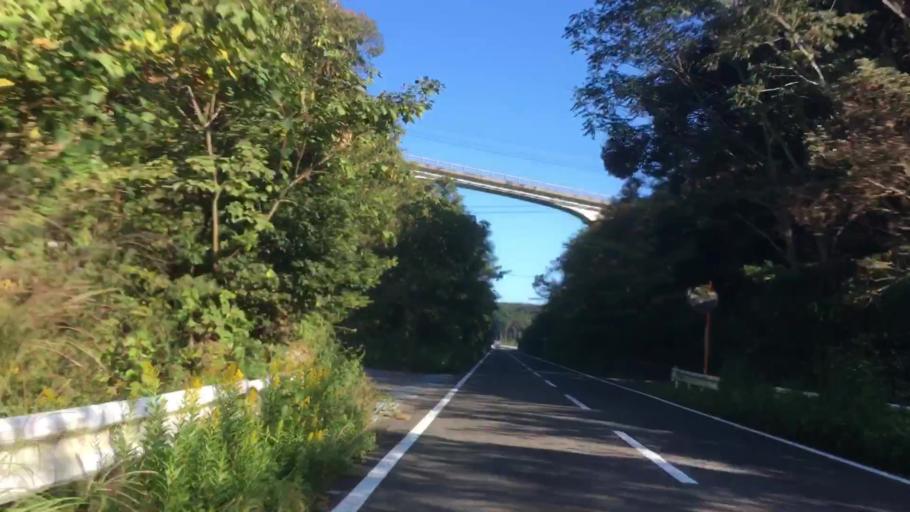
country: JP
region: Nagasaki
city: Sasebo
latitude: 33.0026
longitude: 129.7074
